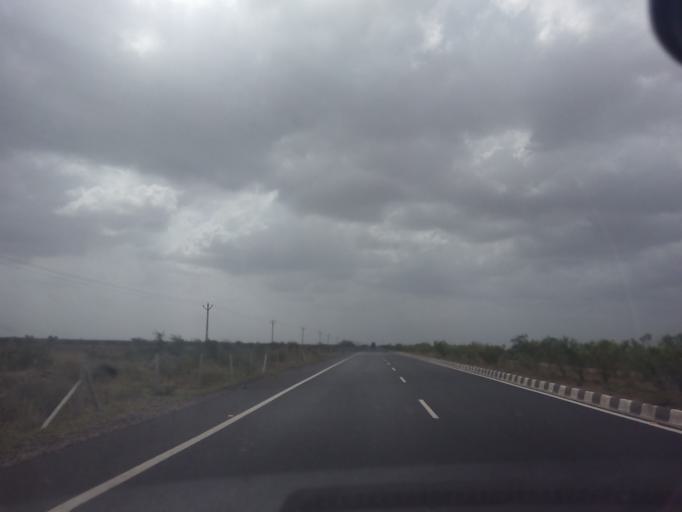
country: IN
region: Gujarat
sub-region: Rajkot
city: Morbi
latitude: 23.0461
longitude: 70.8908
